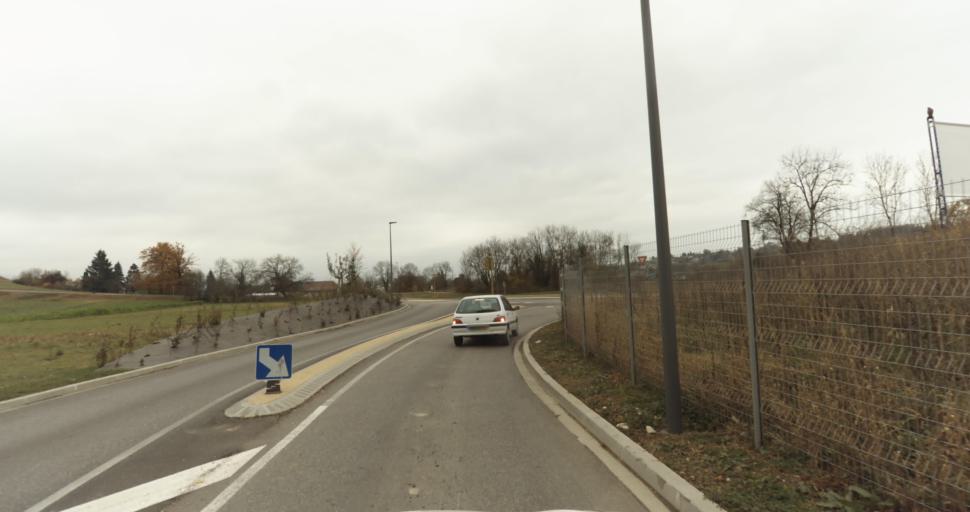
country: FR
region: Rhone-Alpes
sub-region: Departement de la Haute-Savoie
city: Viuz-la-Chiesaz
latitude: 45.8439
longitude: 6.0616
